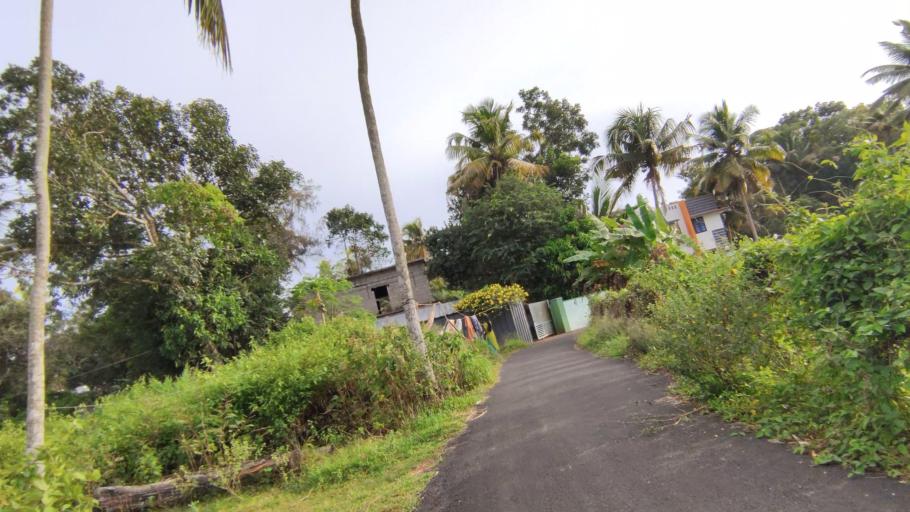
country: IN
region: Kerala
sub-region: Alappuzha
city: Shertallai
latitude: 9.6214
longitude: 76.3376
